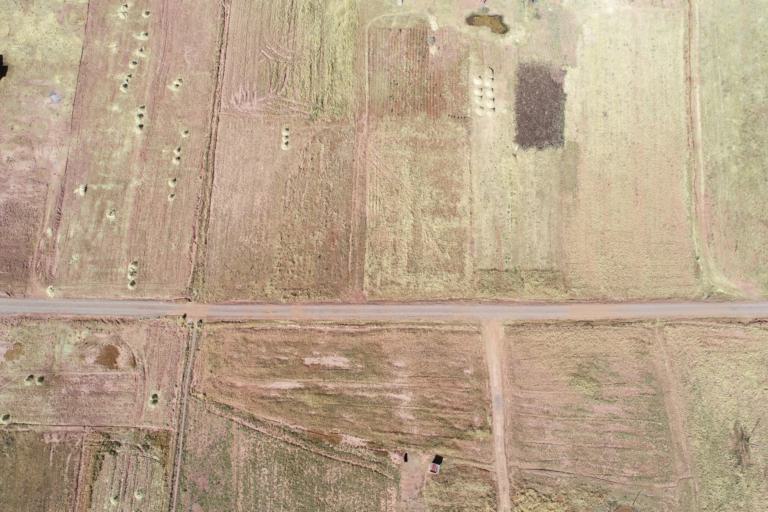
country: BO
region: La Paz
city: Tiahuanaco
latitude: -16.5938
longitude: -68.7552
